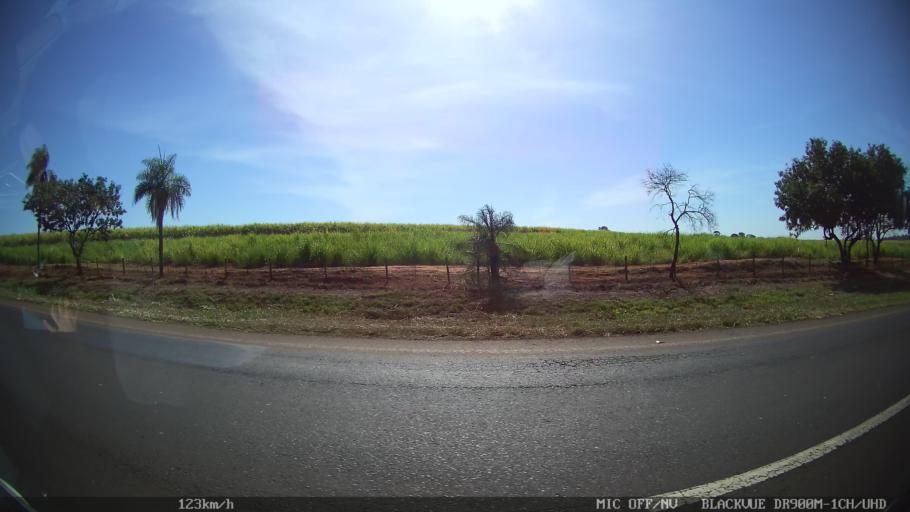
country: BR
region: Sao Paulo
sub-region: Barretos
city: Barretos
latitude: -20.5633
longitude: -48.6572
